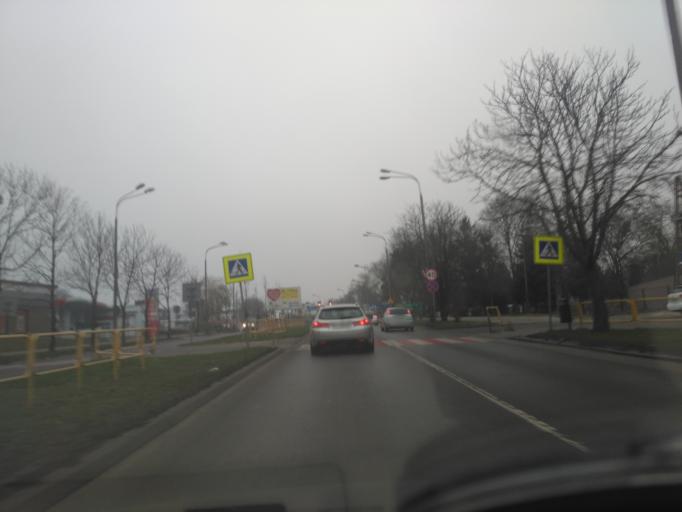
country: PL
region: Lublin Voivodeship
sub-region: Chelm
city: Chelm
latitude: 51.1302
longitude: 23.4681
